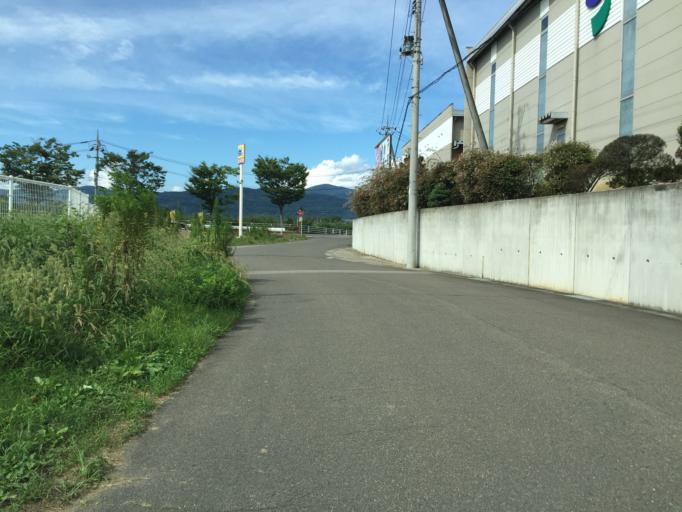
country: JP
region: Fukushima
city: Hobaramachi
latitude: 37.7979
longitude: 140.5004
